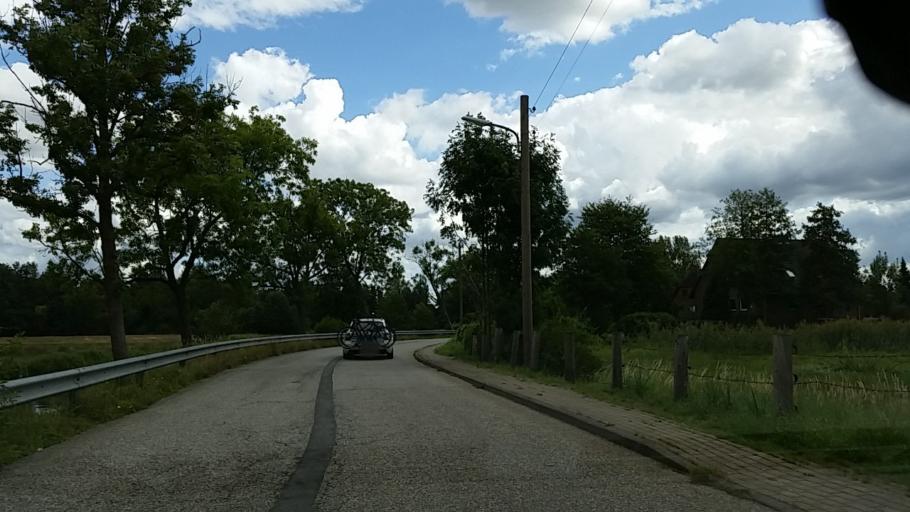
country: DE
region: Schleswig-Holstein
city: Escheburg
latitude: 53.4498
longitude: 10.2903
